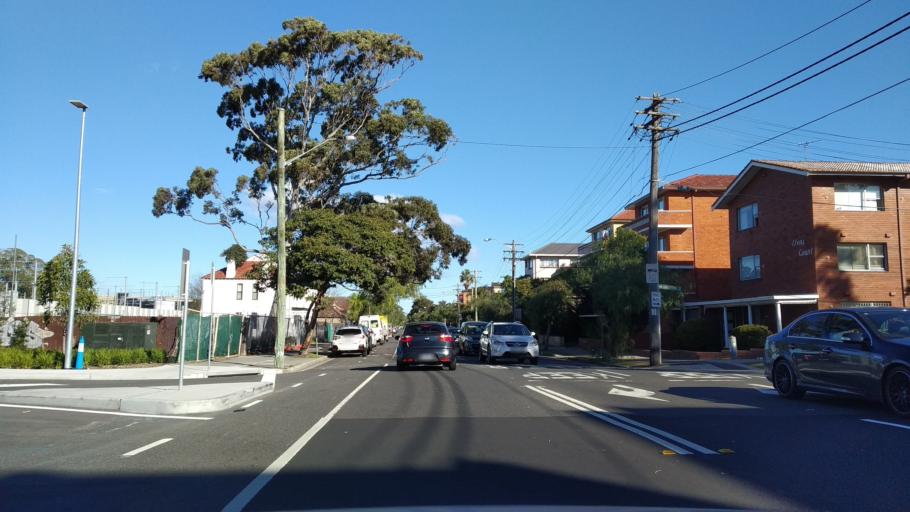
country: AU
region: New South Wales
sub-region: Randwick
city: Kensington
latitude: -33.9047
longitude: 151.2264
